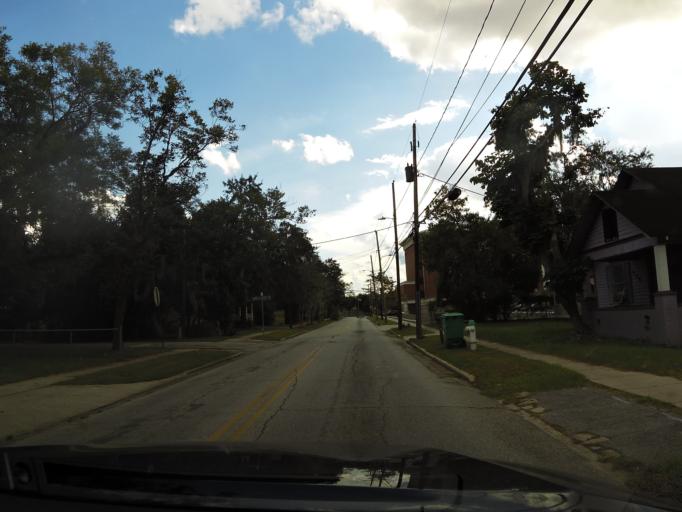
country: US
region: Georgia
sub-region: Lowndes County
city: Valdosta
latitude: 30.8361
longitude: -83.2781
